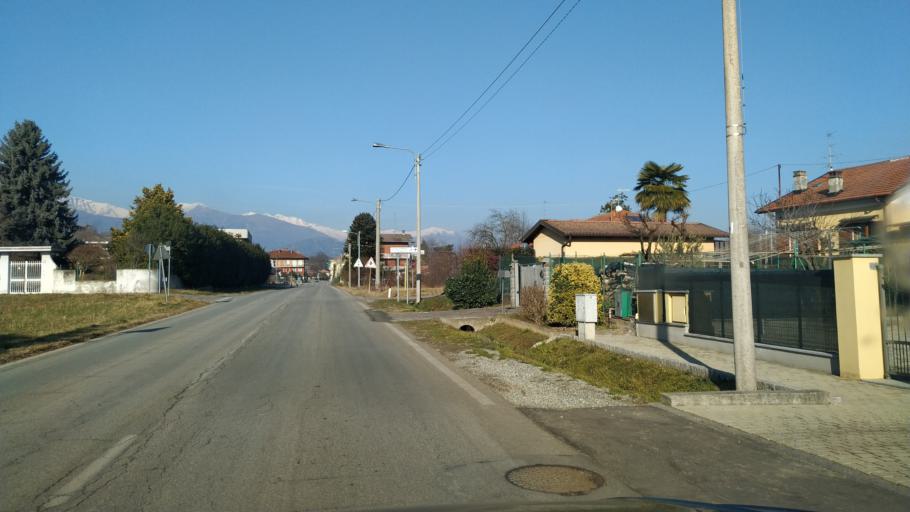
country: IT
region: Piedmont
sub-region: Provincia di Biella
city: Mongrando
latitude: 45.5290
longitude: 8.0106
